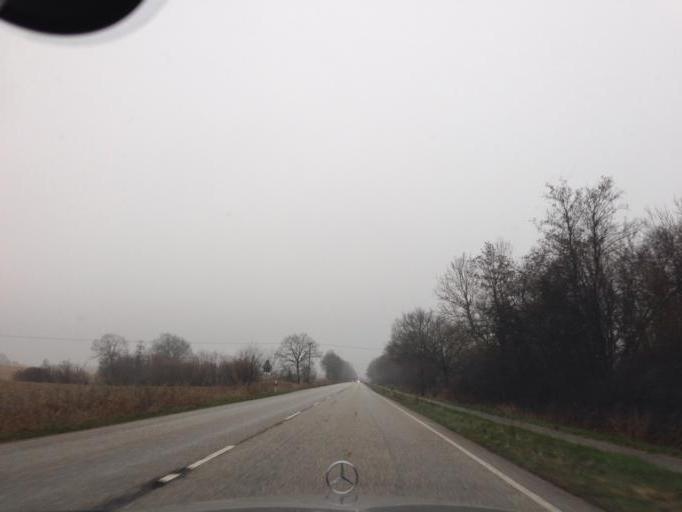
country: DE
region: Schleswig-Holstein
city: Klein Barkau
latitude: 54.2340
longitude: 10.1462
